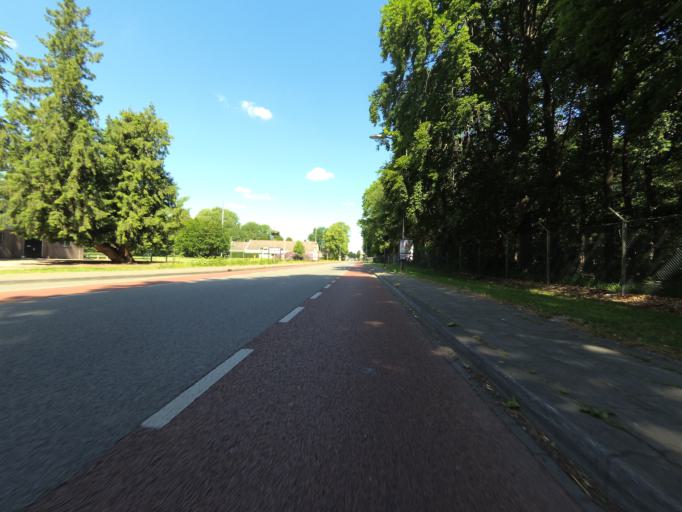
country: NL
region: Gelderland
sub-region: Gemeente Ede
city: Harskamp
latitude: 52.1250
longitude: 5.7581
